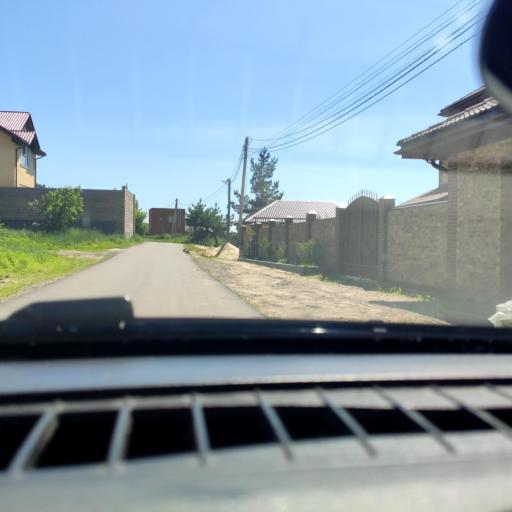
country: RU
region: Voronezj
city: Podgornoye
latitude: 51.7942
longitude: 39.1354
